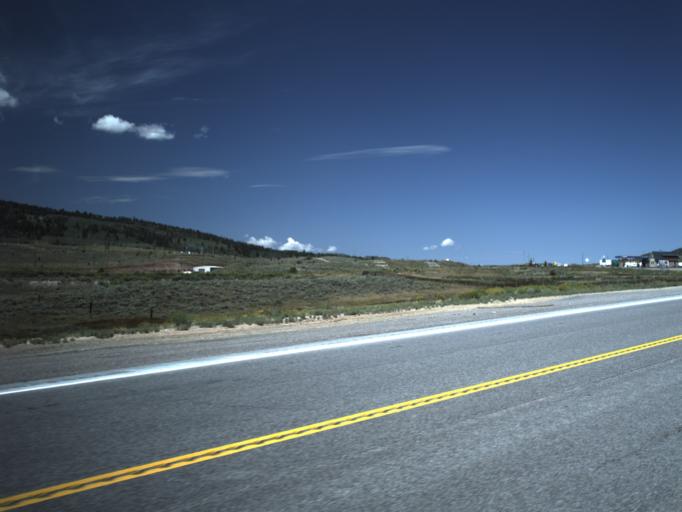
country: US
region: Utah
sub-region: Carbon County
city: Helper
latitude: 39.9273
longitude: -111.0739
